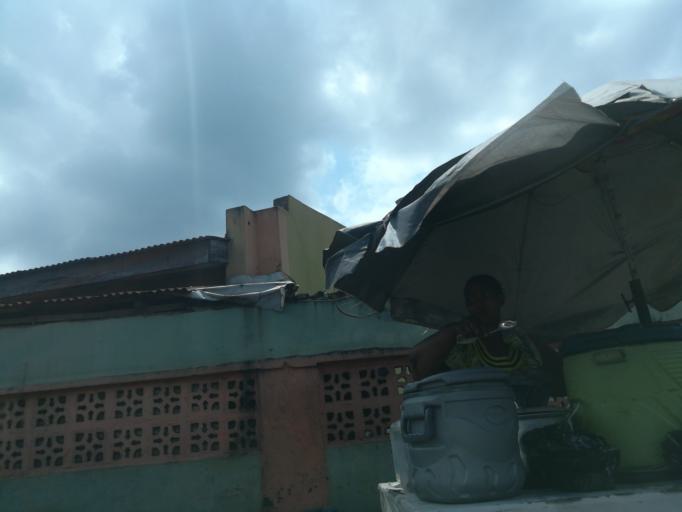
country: NG
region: Lagos
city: Mushin
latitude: 6.5333
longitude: 3.3639
